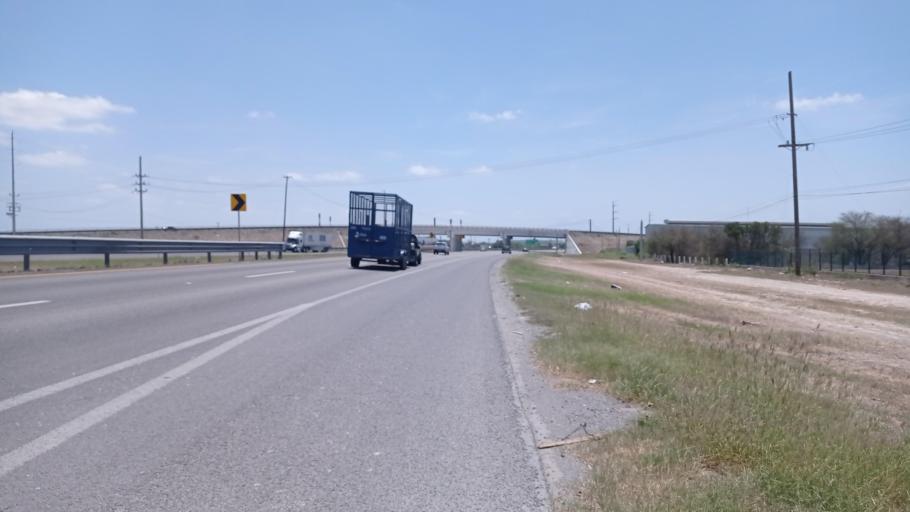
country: MX
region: Nuevo Leon
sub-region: Apodaca
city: Entronque Laredo-Salinas Victoria
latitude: 25.8875
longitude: -100.2213
